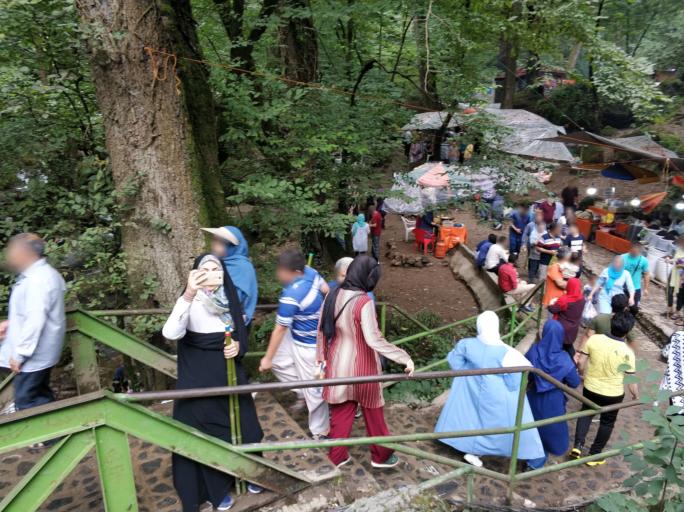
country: IR
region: Gilan
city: Fuman
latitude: 37.0709
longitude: 49.2483
